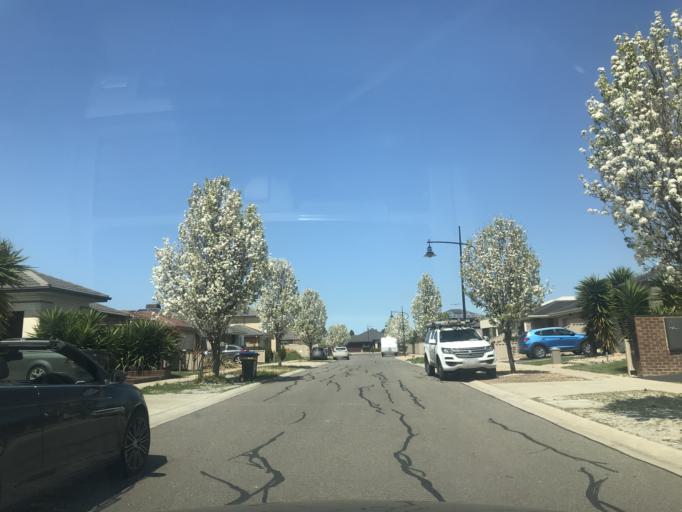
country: AU
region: Victoria
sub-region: Wyndham
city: Hoppers Crossing
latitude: -37.8875
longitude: 144.7214
